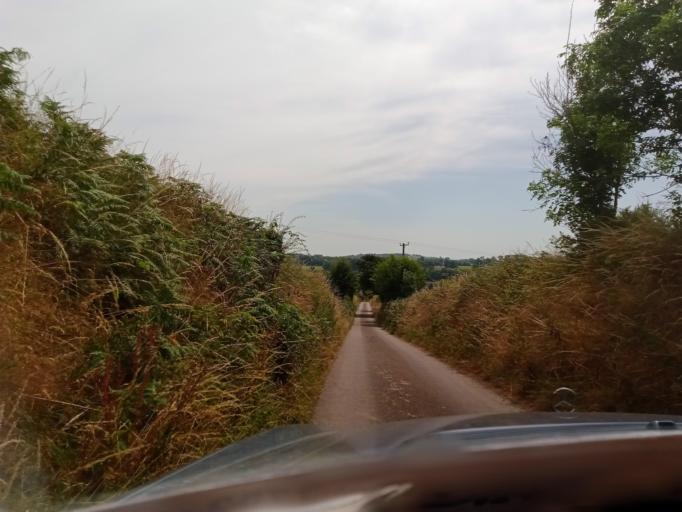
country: IE
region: Leinster
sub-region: Kilkenny
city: Mooncoin
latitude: 52.2509
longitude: -7.2144
